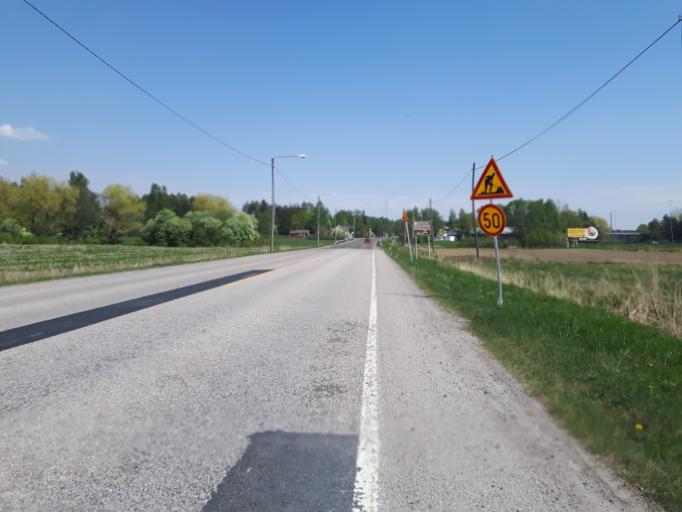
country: FI
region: Uusimaa
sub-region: Helsinki
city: Nickby
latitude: 60.3099
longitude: 25.3844
